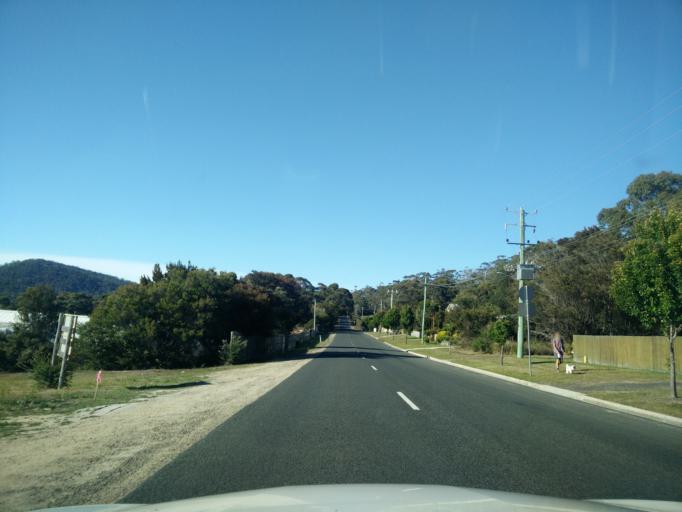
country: AU
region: Tasmania
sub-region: Break O'Day
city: St Helens
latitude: -41.8808
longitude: 148.3022
